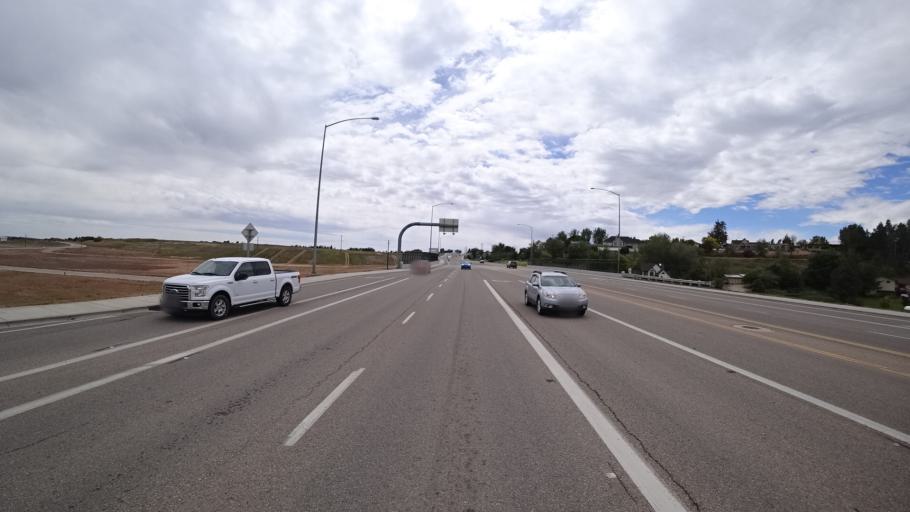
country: US
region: Idaho
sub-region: Ada County
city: Meridian
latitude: 43.5925
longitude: -116.4340
